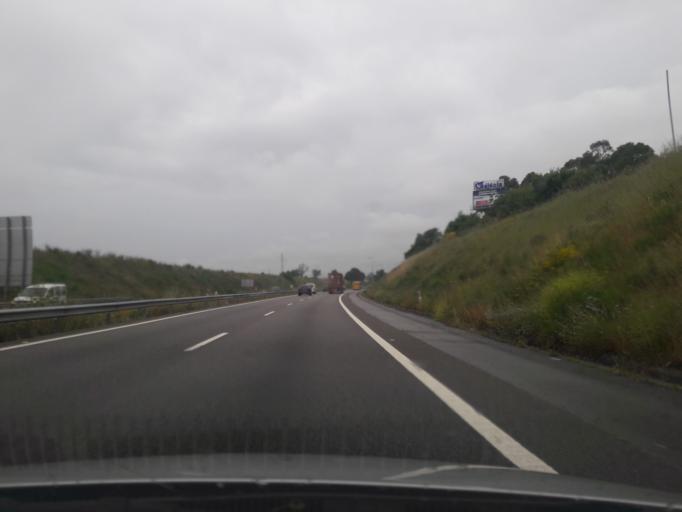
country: PT
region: Porto
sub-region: Vila do Conde
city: Arvore
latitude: 41.3208
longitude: -8.7064
